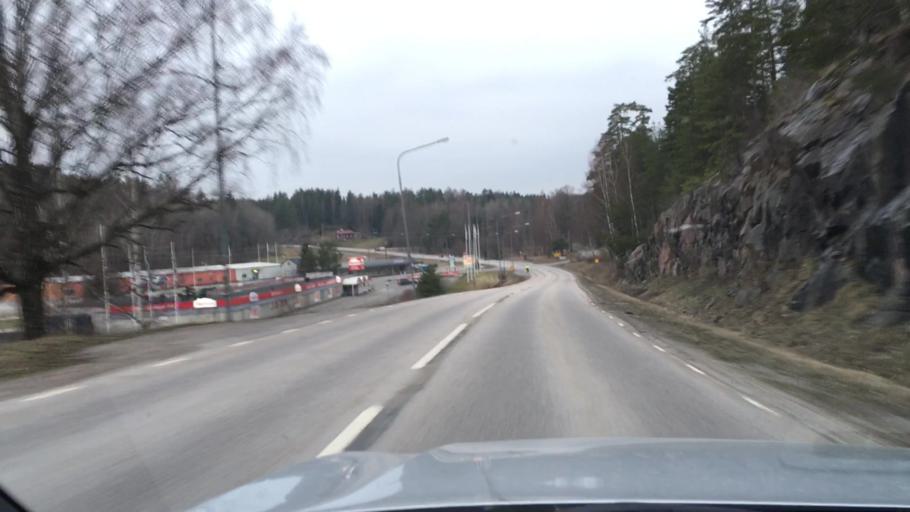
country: SE
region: OEstergoetland
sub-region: Valdemarsviks Kommun
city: Valdemarsvik
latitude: 58.2155
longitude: 16.5800
